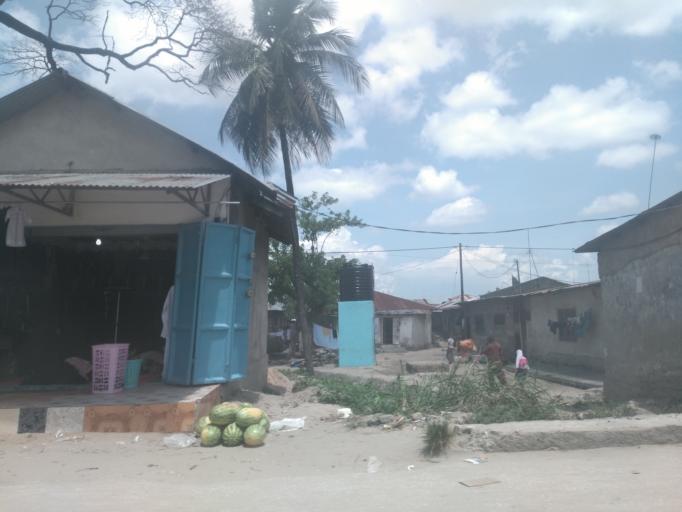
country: TZ
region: Zanzibar Urban/West
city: Zanzibar
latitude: -6.1632
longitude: 39.2175
